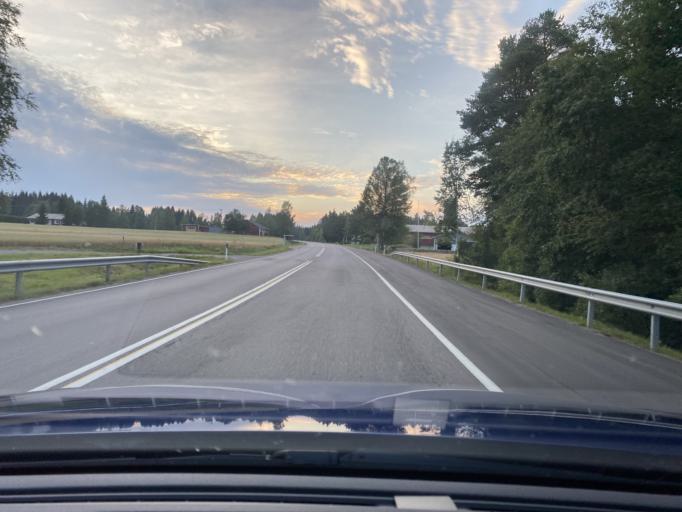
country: FI
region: Satakunta
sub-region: Pohjois-Satakunta
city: Kankaanpaeae
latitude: 61.8554
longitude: 22.3264
